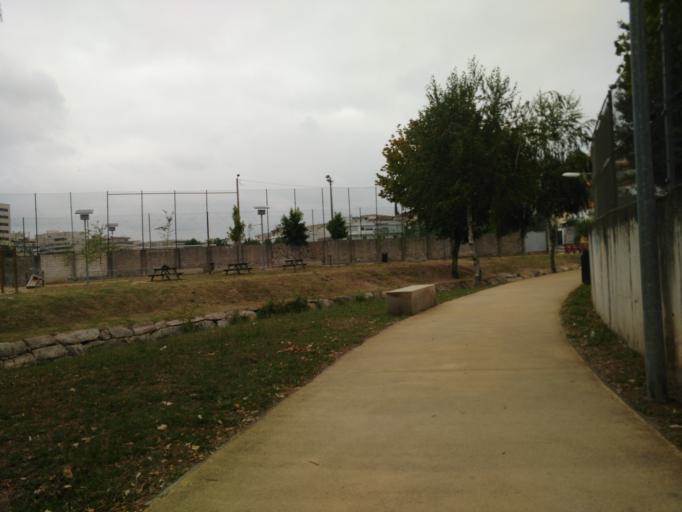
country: PT
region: Braga
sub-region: Braga
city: Braga
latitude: 41.5386
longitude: -8.4309
